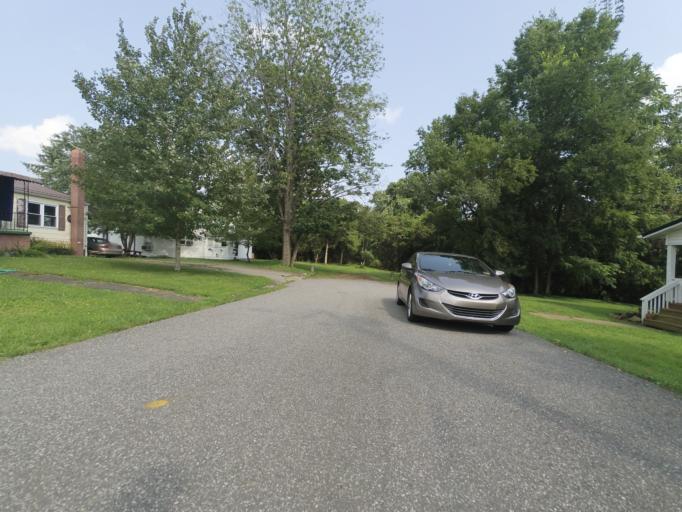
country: US
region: West Virginia
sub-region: Cabell County
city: Huntington
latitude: 38.4030
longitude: -82.3995
